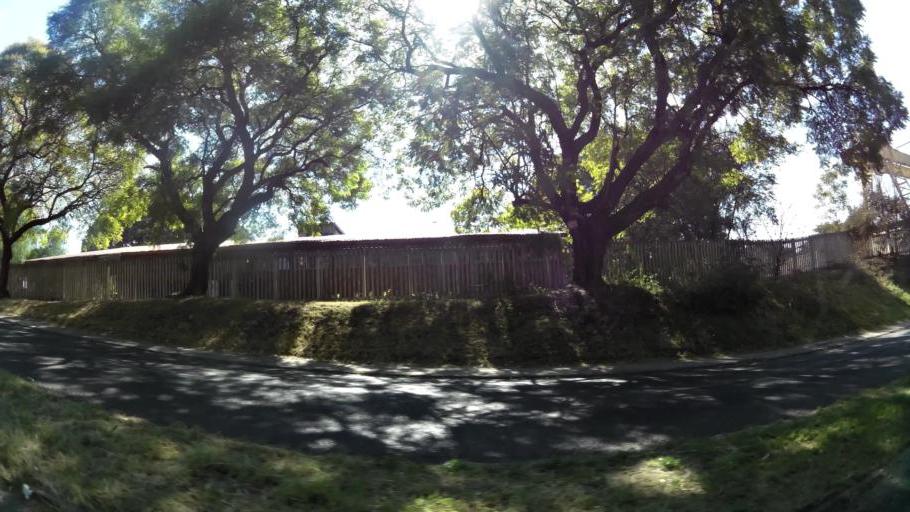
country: ZA
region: Gauteng
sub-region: City of Tshwane Metropolitan Municipality
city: Pretoria
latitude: -25.7557
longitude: 28.1465
